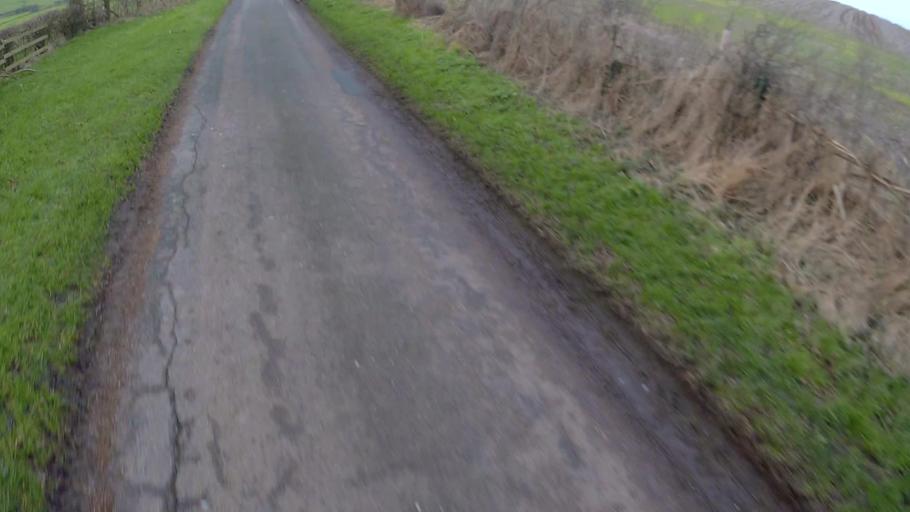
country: GB
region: England
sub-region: Lincolnshire
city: Bourne
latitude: 52.8279
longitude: -0.4631
